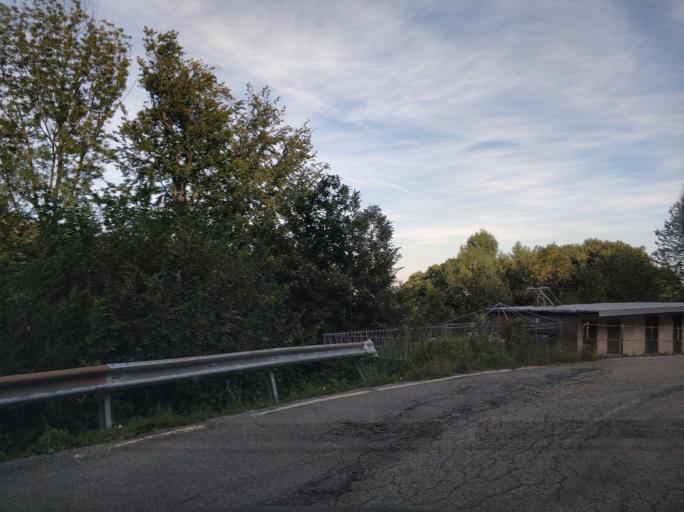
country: IT
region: Piedmont
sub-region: Provincia di Torino
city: Monastero di Lanzo
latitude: 45.3043
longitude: 7.4447
